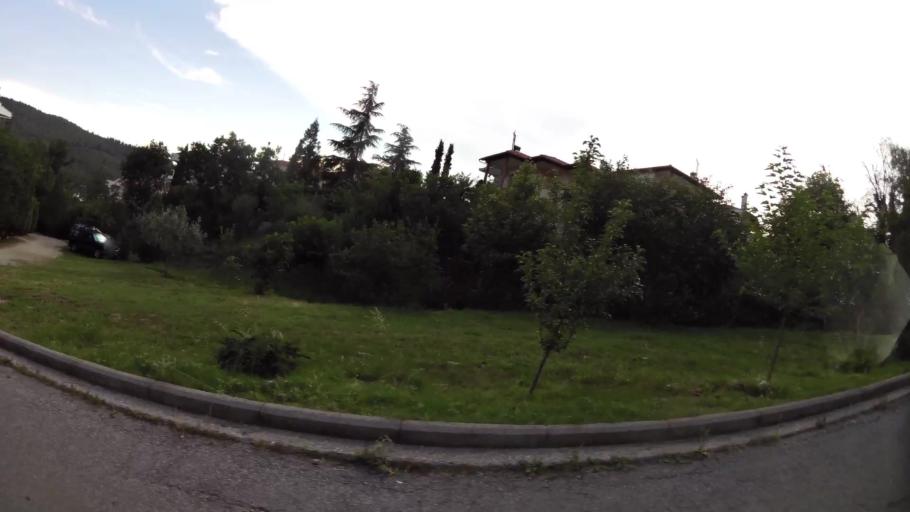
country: GR
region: Central Macedonia
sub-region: Nomos Thessalonikis
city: Pefka
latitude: 40.6540
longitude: 22.9998
